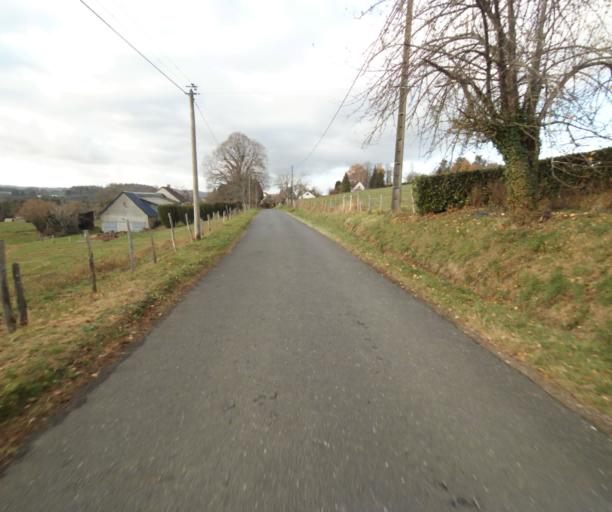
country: FR
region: Limousin
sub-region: Departement de la Correze
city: Laguenne
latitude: 45.2322
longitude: 1.7909
